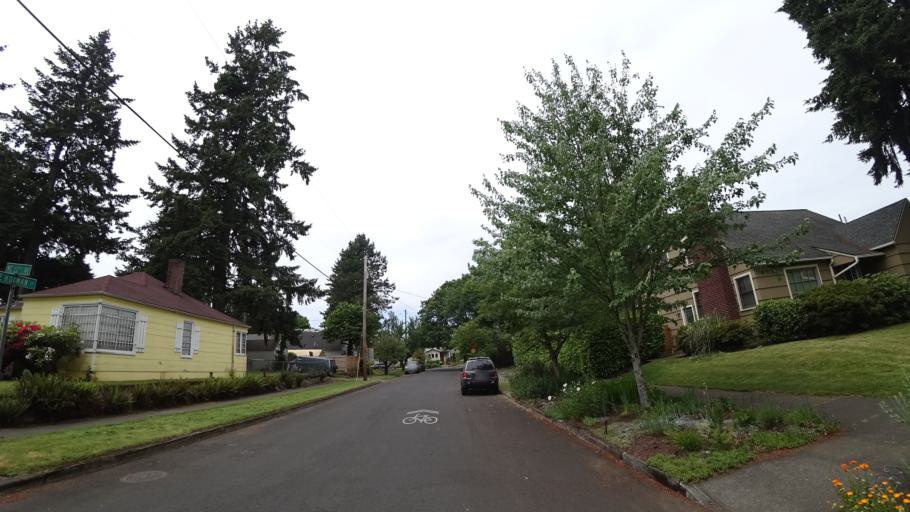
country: US
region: Oregon
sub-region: Multnomah County
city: Portland
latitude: 45.5682
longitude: -122.6436
